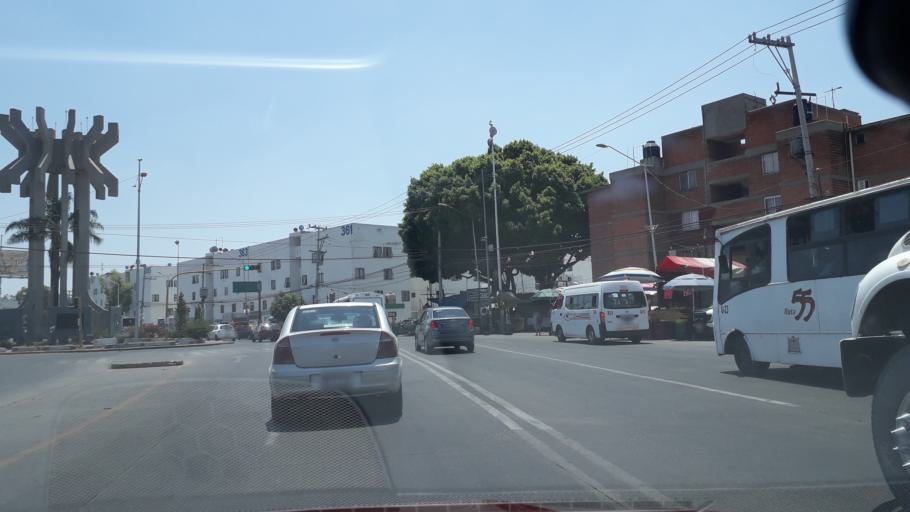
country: MX
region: Puebla
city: Puebla
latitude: 19.0100
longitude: -98.1881
